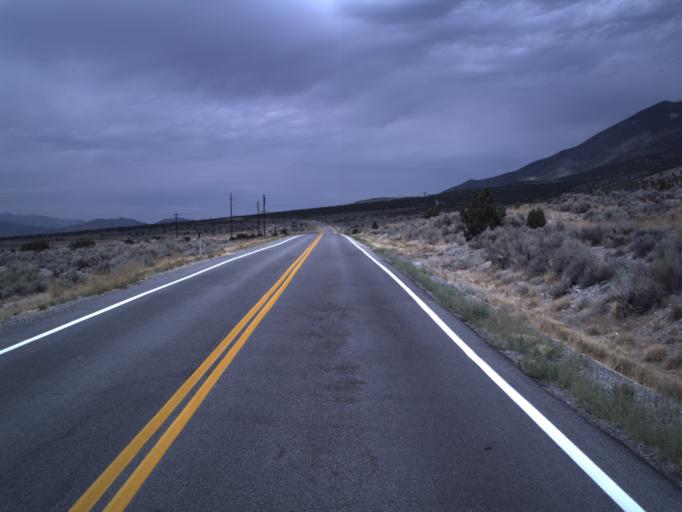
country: US
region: Utah
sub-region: Tooele County
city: Tooele
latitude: 40.3143
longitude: -112.2832
